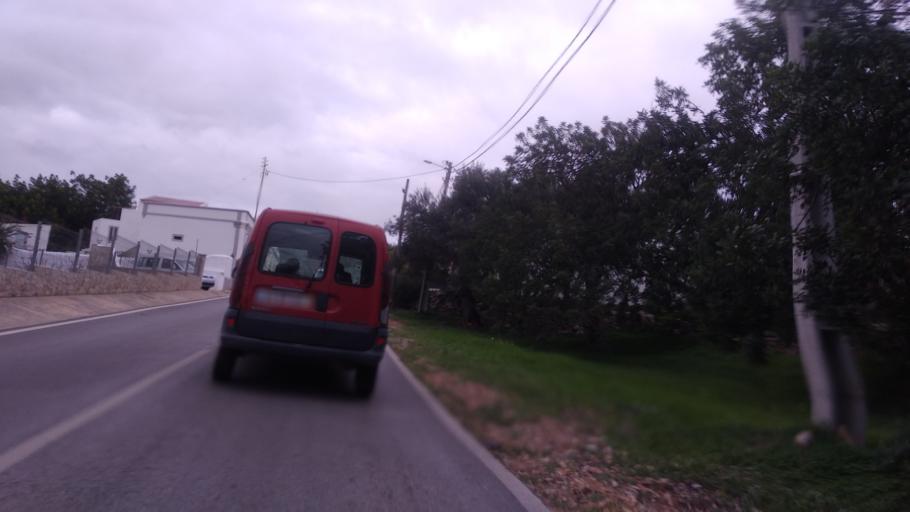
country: PT
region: Faro
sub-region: Faro
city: Santa Barbara de Nexe
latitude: 37.1088
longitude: -7.9619
